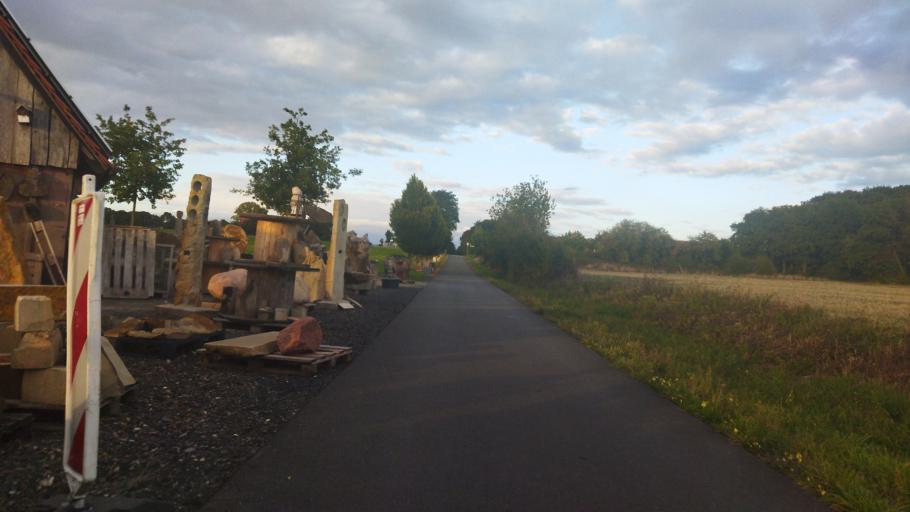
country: DE
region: North Rhine-Westphalia
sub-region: Regierungsbezirk Munster
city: Billerbeck
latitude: 52.0057
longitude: 7.2552
